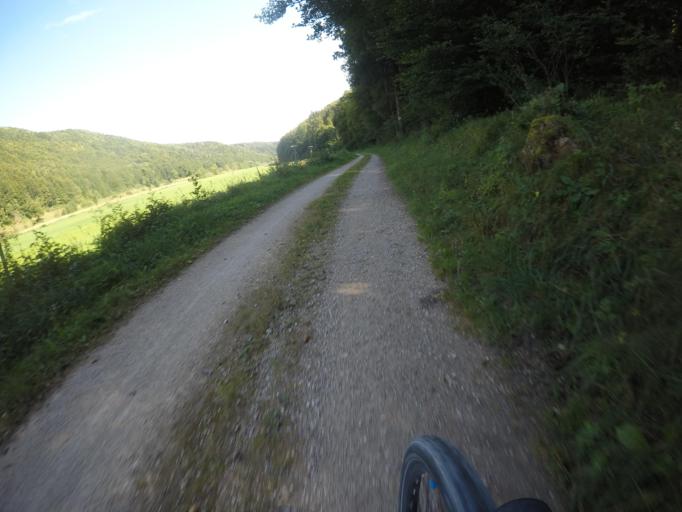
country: DE
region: Baden-Wuerttemberg
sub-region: Tuebingen Region
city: Schelklingen
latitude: 48.3668
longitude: 9.6885
